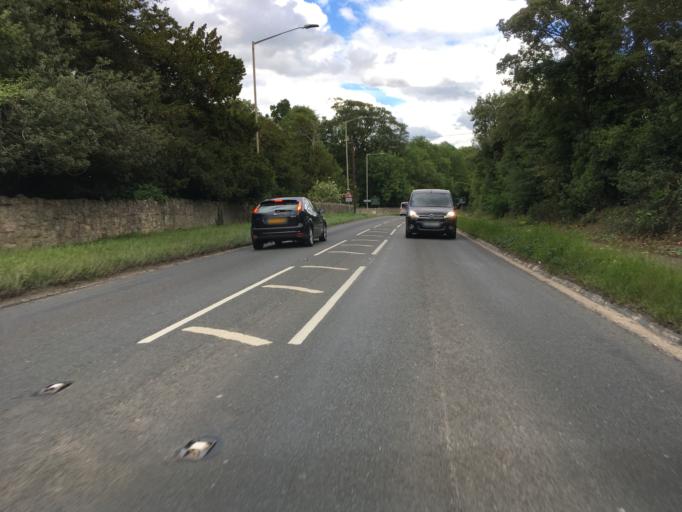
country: GB
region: England
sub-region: Buckinghamshire
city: Stone
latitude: 51.8030
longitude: -0.8509
